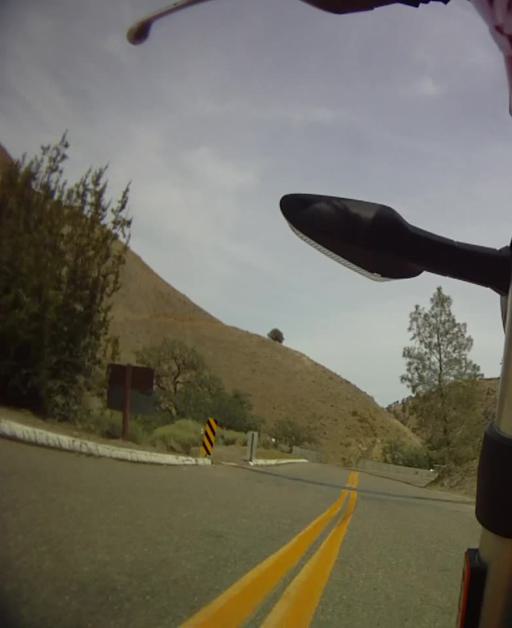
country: US
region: California
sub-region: Stanislaus County
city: Patterson
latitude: 37.4377
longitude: -121.3303
